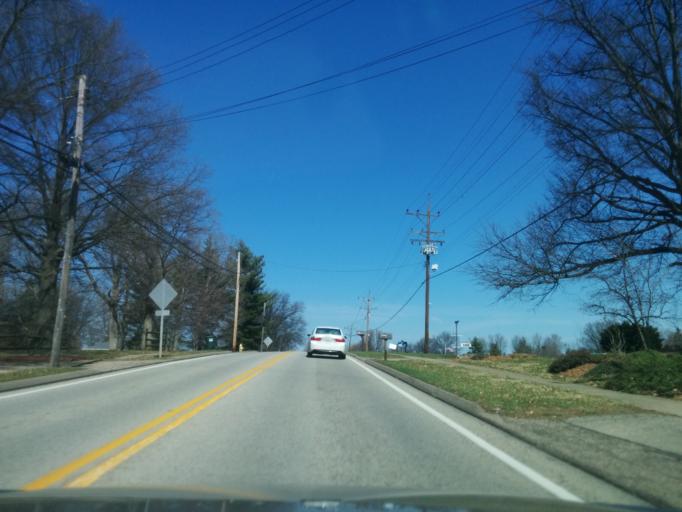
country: US
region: Ohio
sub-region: Hamilton County
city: Groesbeck
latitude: 39.2325
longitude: -84.5991
